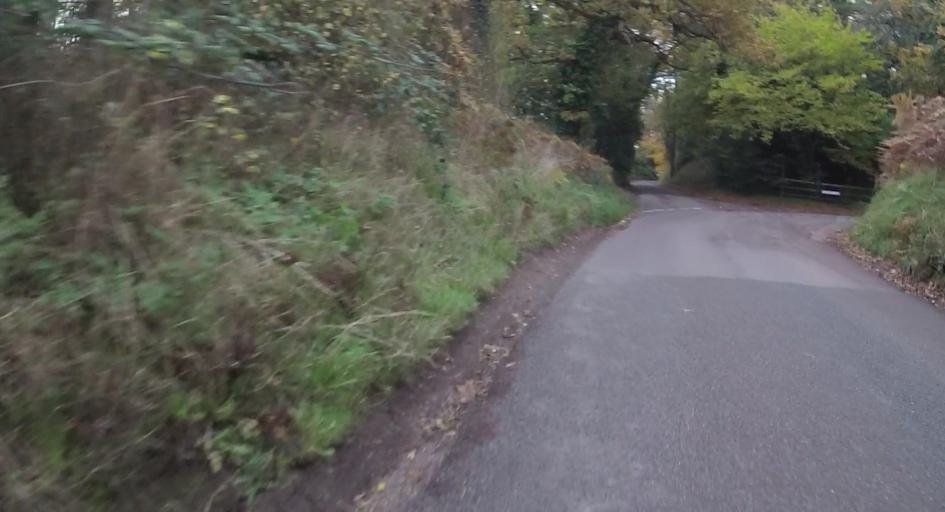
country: GB
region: England
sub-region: Surrey
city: Churt
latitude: 51.1483
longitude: -0.7988
